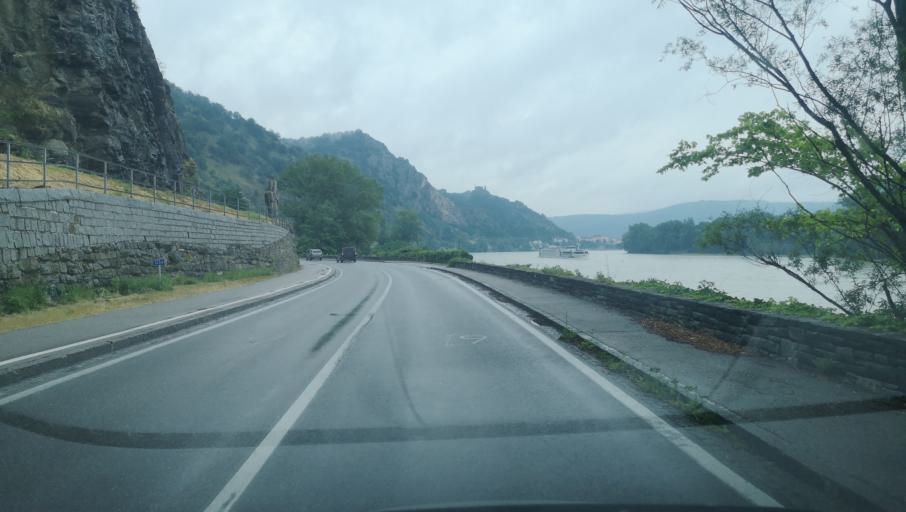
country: AT
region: Lower Austria
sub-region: Politischer Bezirk Krems
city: Durnstein
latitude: 48.4094
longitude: 15.5053
